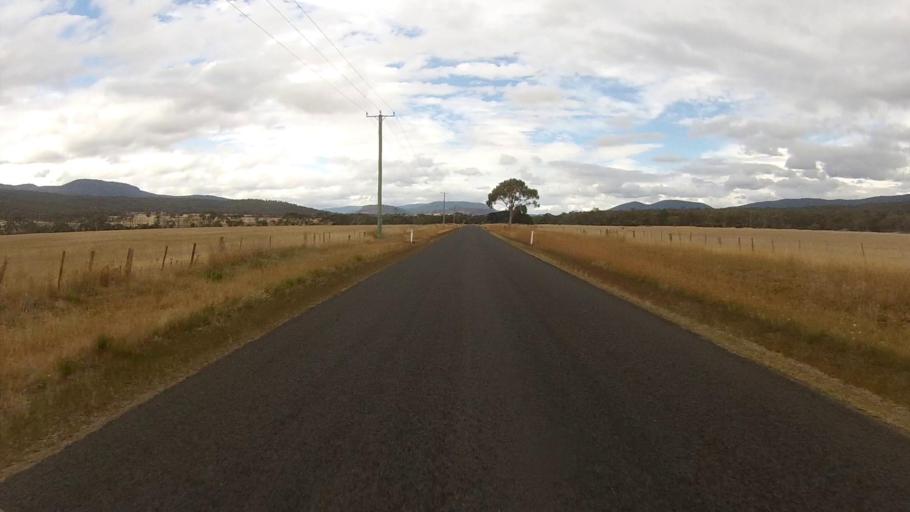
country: AU
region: Tasmania
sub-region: Break O'Day
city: St Helens
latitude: -41.8224
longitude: 147.8787
